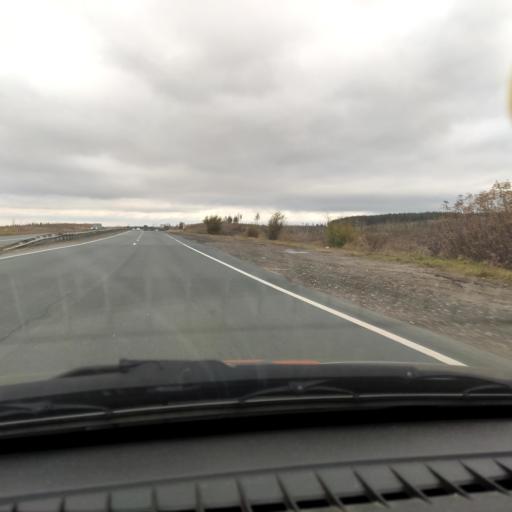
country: RU
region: Samara
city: Zhigulevsk
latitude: 53.5038
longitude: 49.5387
